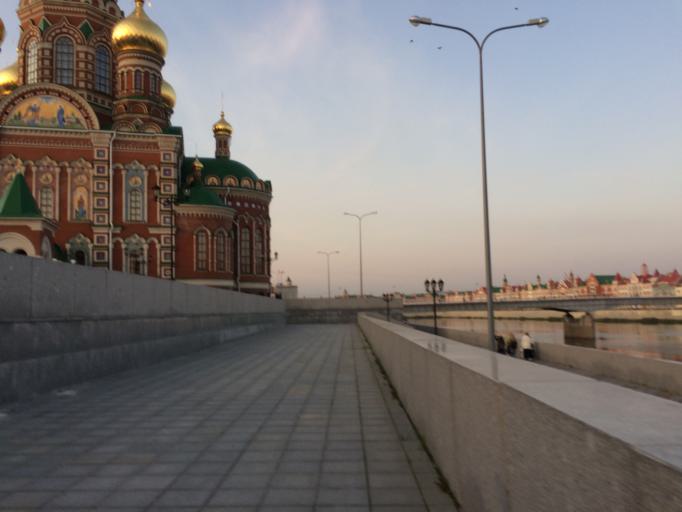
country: RU
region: Mariy-El
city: Yoshkar-Ola
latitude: 56.6322
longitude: 47.9042
